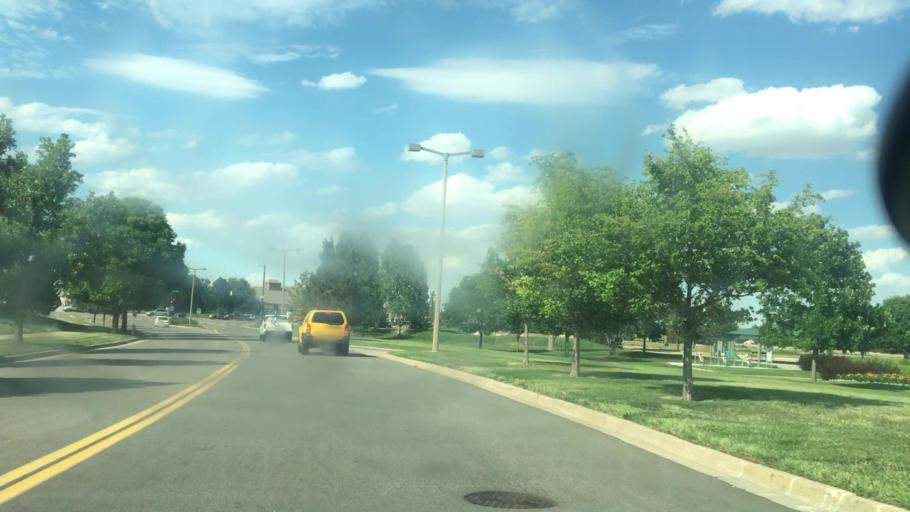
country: US
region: Colorado
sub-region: Douglas County
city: Meridian
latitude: 39.5346
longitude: -104.8435
